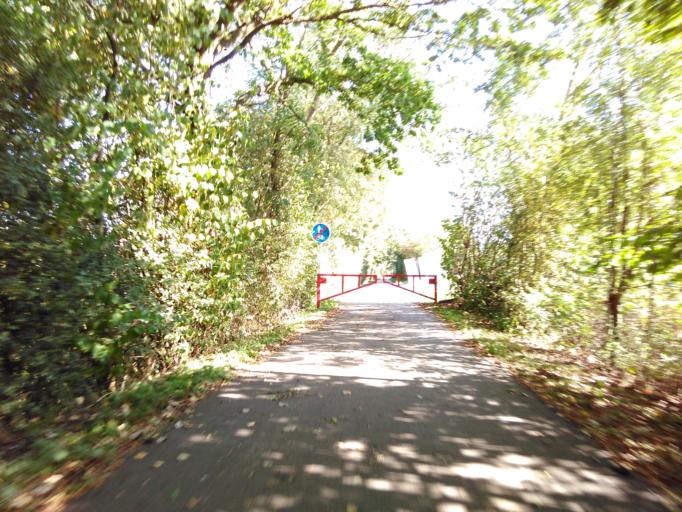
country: LU
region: Diekirch
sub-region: Canton de Redange
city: Beckerich
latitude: 49.7291
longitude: 5.9020
